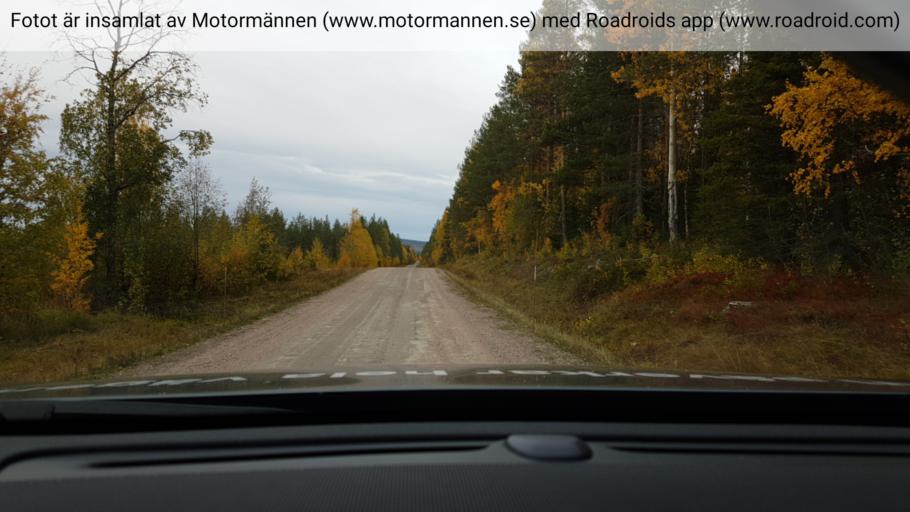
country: SE
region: Norrbotten
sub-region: Overkalix Kommun
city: OEverkalix
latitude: 66.2665
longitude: 23.0157
